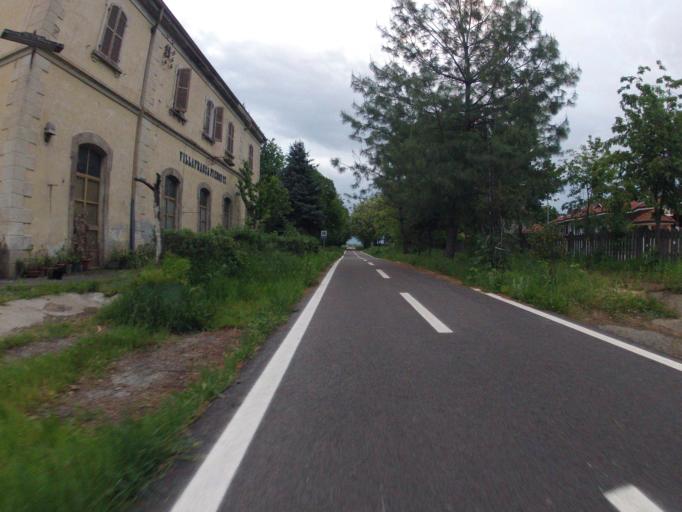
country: IT
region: Piedmont
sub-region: Provincia di Torino
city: Villafranca Piemonte
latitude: 44.7870
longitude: 7.5099
